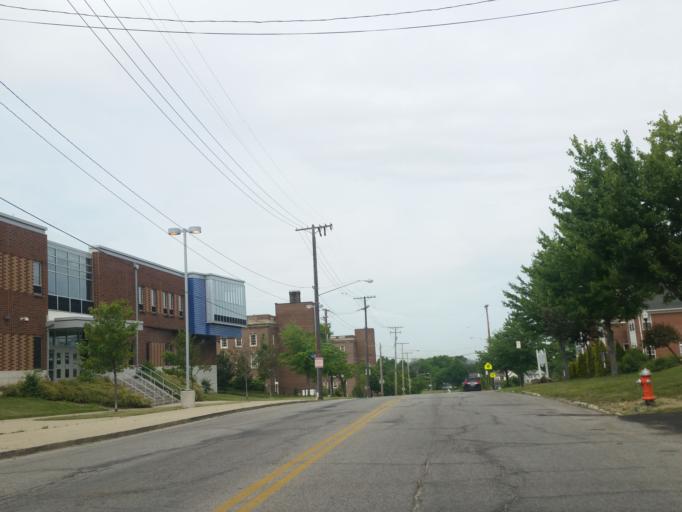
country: US
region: Ohio
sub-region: Cuyahoga County
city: East Cleveland
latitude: 41.4858
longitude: -81.6036
